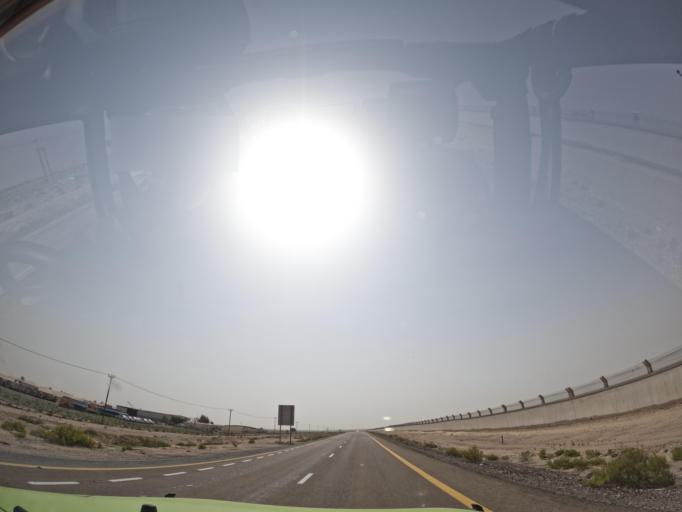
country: AE
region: Dubai
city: Dubai
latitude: 24.6660
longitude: 55.1774
